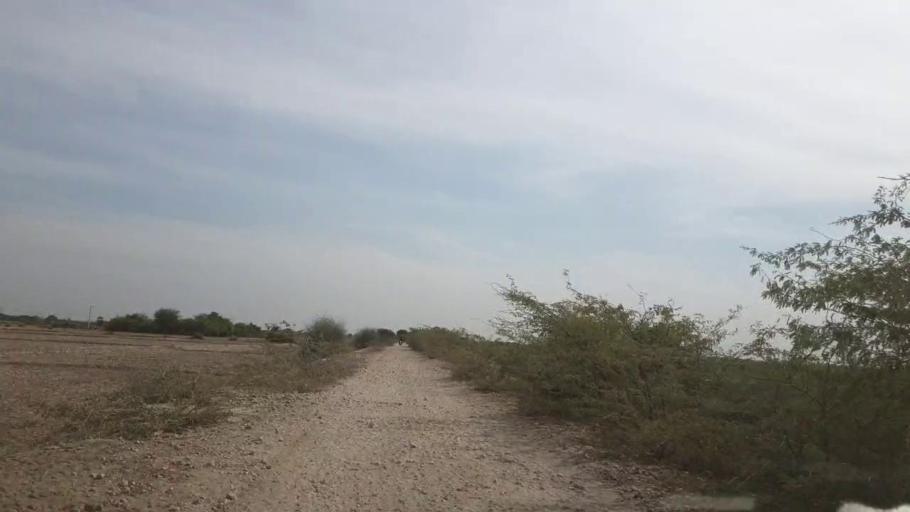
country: PK
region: Sindh
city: Nabisar
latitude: 25.0437
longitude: 69.5616
